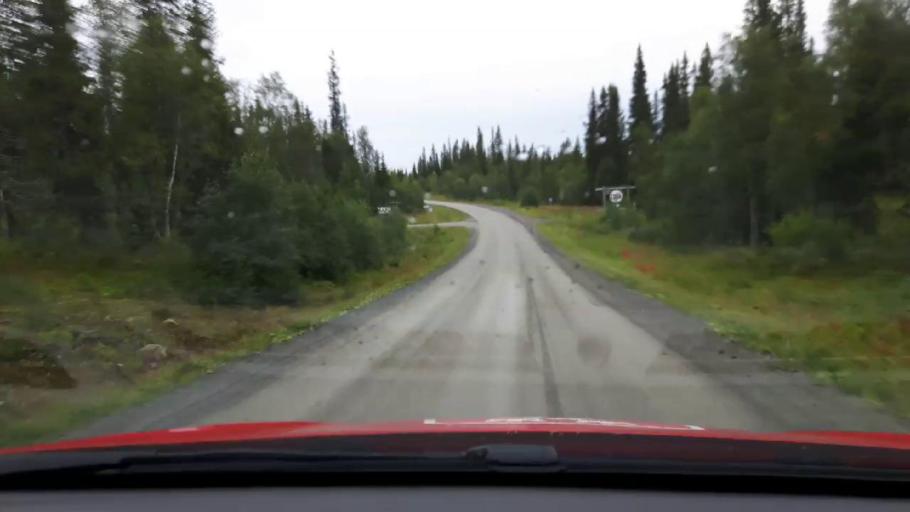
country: SE
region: Jaemtland
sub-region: Are Kommun
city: Are
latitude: 63.4034
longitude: 13.1999
